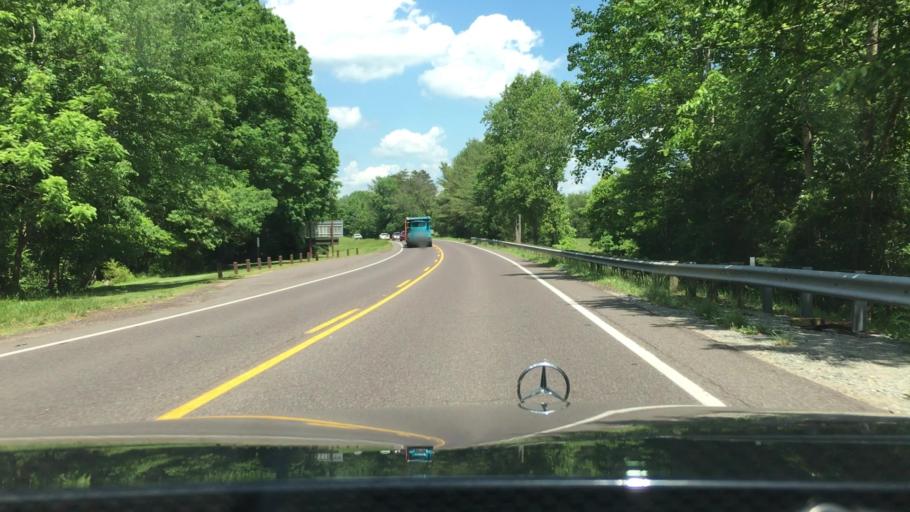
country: US
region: Virginia
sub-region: Spotsylvania County
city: Spotsylvania
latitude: 38.3220
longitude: -77.7345
